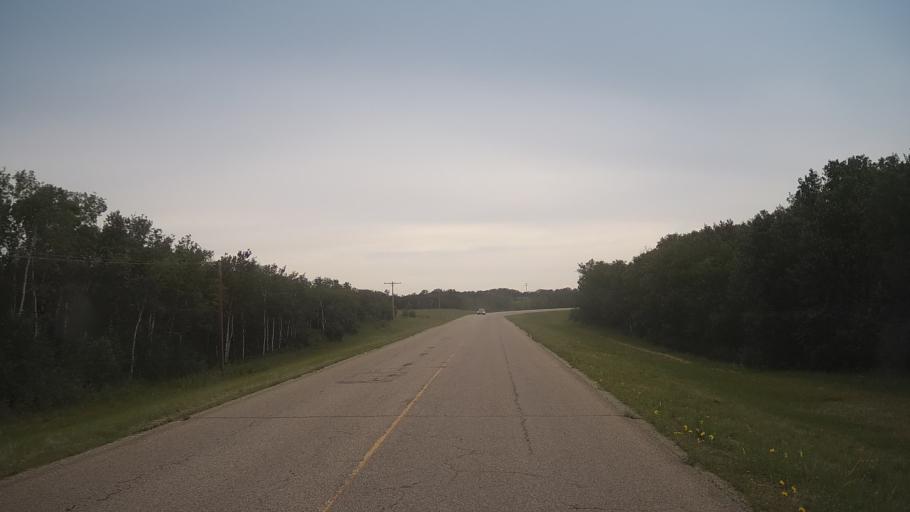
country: CA
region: Saskatchewan
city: Saskatoon
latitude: 51.8490
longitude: -106.5311
